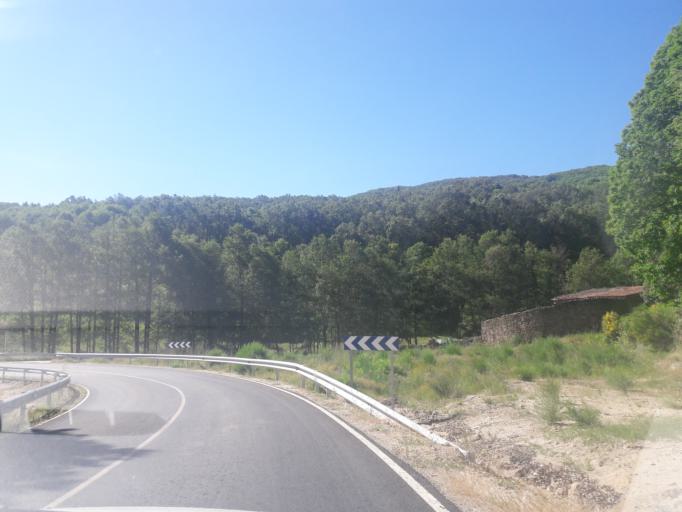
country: ES
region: Castille and Leon
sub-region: Provincia de Salamanca
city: Penacaballera
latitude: 40.3415
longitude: -5.8748
